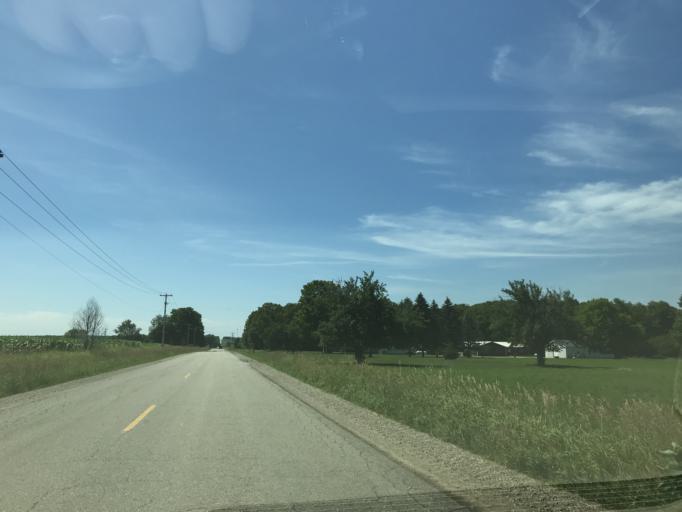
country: US
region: Michigan
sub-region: Missaukee County
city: Lake City
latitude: 44.3265
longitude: -85.0750
